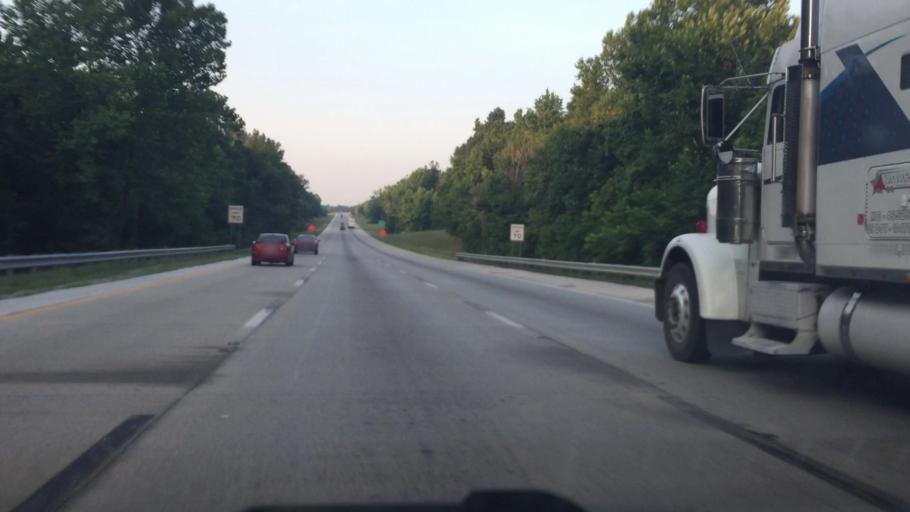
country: US
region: North Carolina
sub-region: Guilford County
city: Jamestown
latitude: 35.9765
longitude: -79.8907
